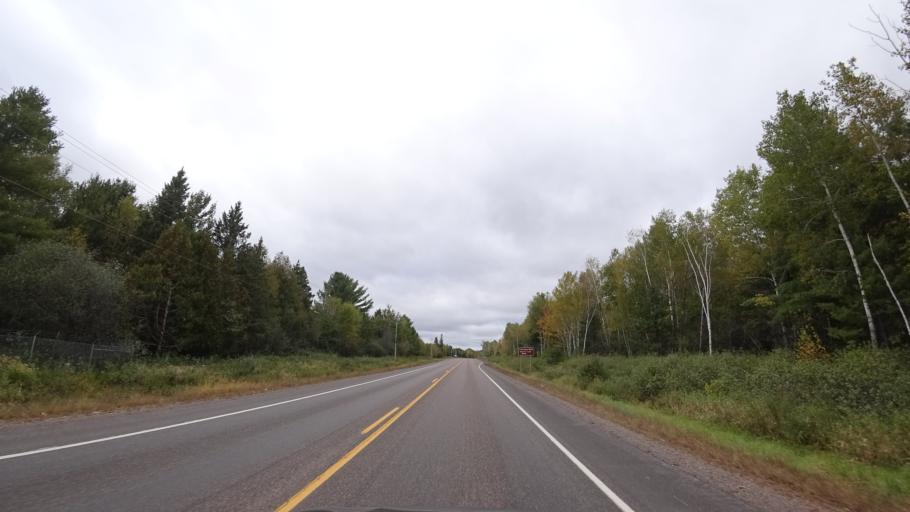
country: US
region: Wisconsin
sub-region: Rusk County
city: Ladysmith
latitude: 45.4419
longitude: -91.1111
